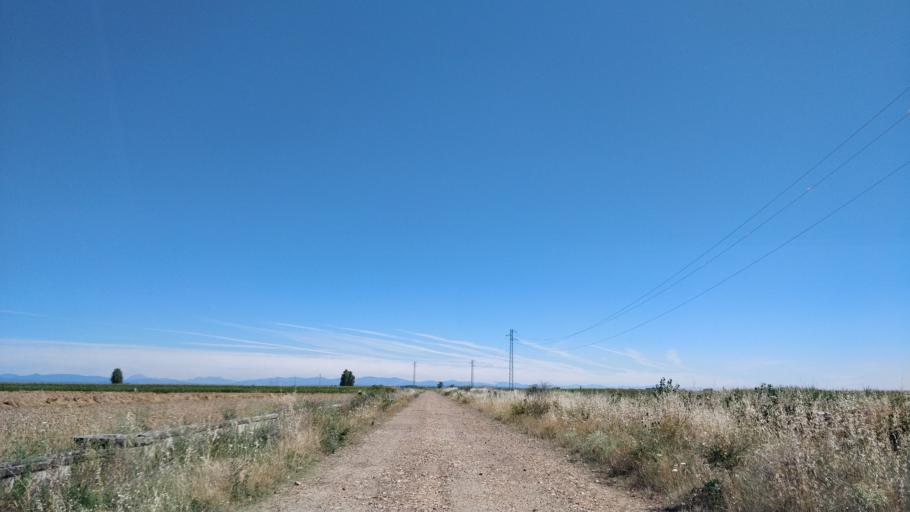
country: ES
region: Castille and Leon
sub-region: Provincia de Leon
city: Bustillo del Paramo
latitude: 42.4349
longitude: -5.8216
